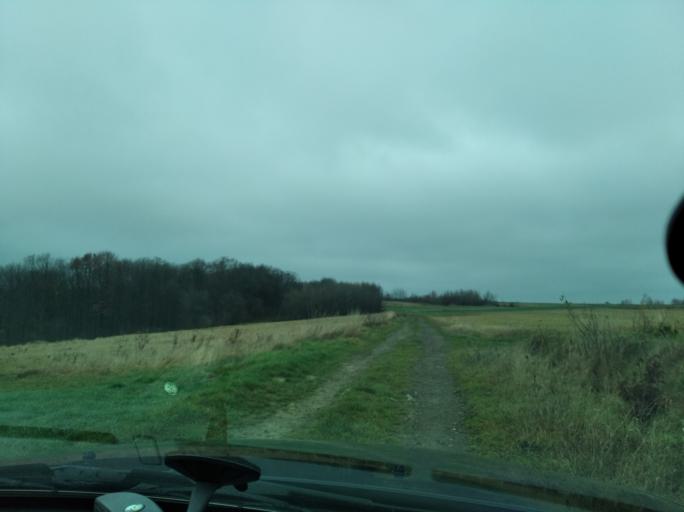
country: PL
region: Subcarpathian Voivodeship
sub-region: Powiat przeworski
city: Jawornik Polski
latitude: 49.8928
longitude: 22.2763
